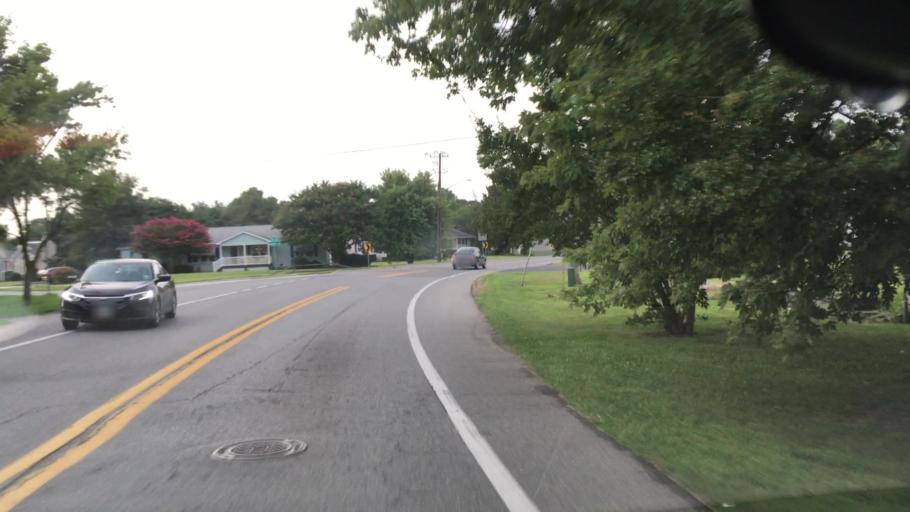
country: US
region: Delaware
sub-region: Sussex County
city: Ocean View
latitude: 38.5371
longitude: -75.0911
